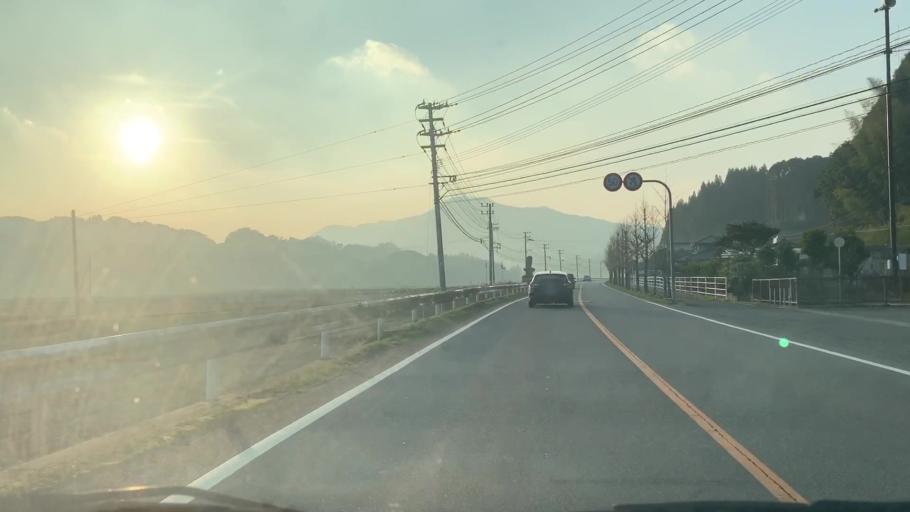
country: JP
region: Saga Prefecture
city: Takeocho-takeo
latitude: 33.2578
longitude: 130.0766
